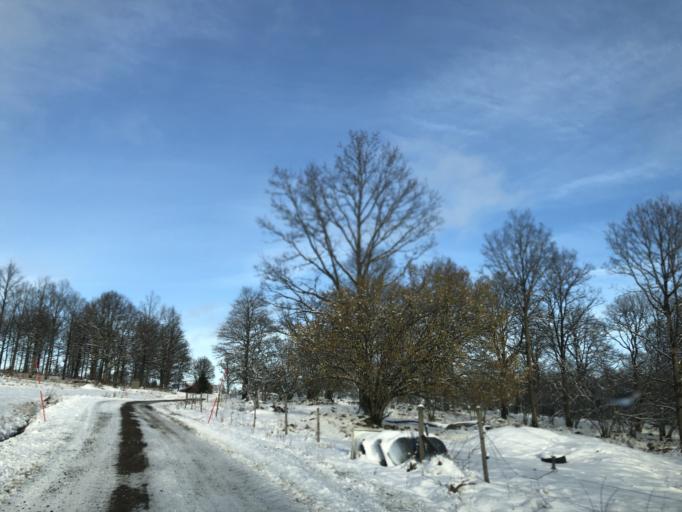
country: SE
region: Vaestra Goetaland
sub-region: Ulricehamns Kommun
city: Ulricehamn
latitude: 57.7324
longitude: 13.4837
